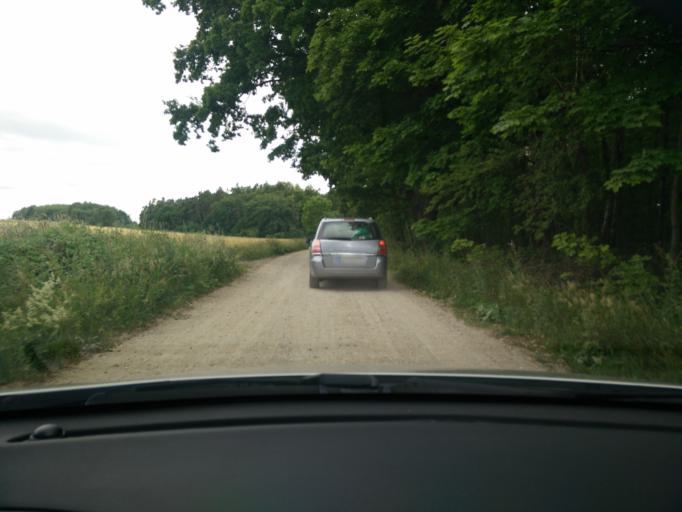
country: PL
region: Pomeranian Voivodeship
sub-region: Powiat pucki
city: Mrzezino
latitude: 54.6609
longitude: 18.4512
